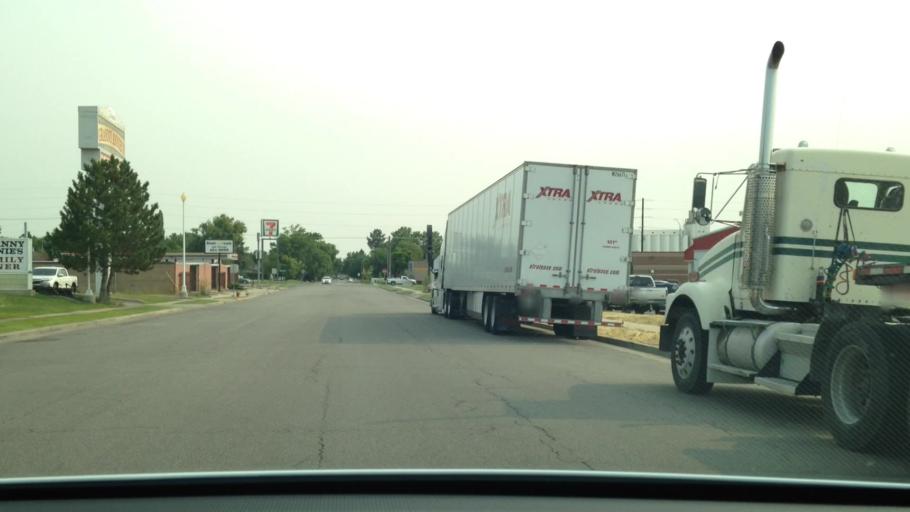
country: US
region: Utah
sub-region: Davis County
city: Kaysville
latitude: 41.0398
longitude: -111.9462
